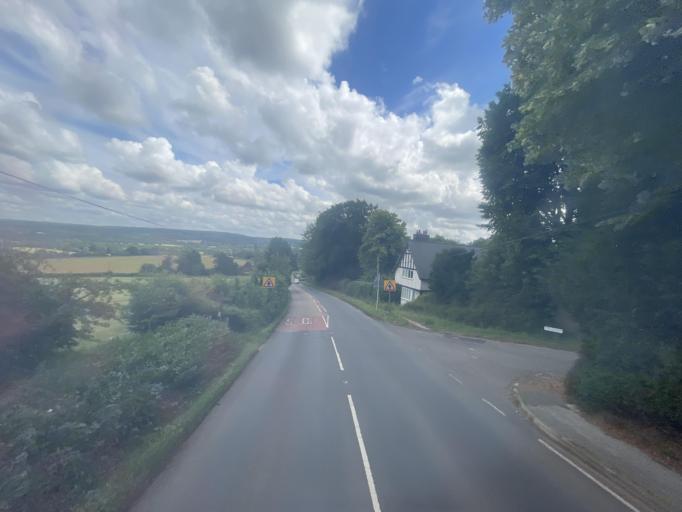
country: GB
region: England
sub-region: Kent
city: Westerham
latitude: 51.2844
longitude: 0.0646
